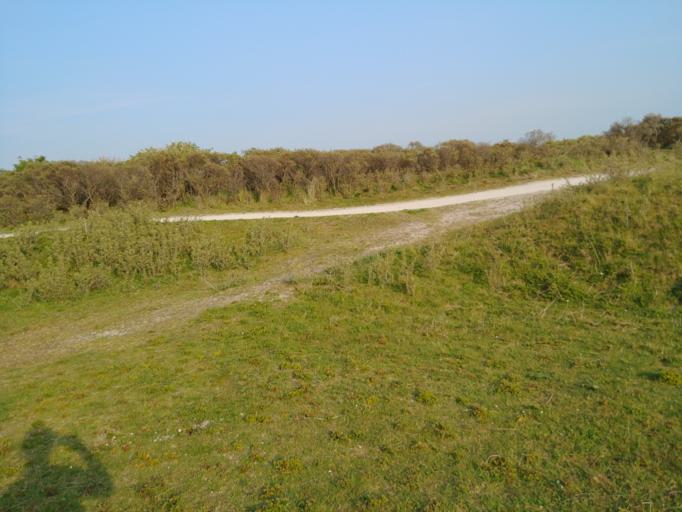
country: NL
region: South Holland
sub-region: Gemeente Katwijk
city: Katwijk aan Zee
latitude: 52.1871
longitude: 4.3877
